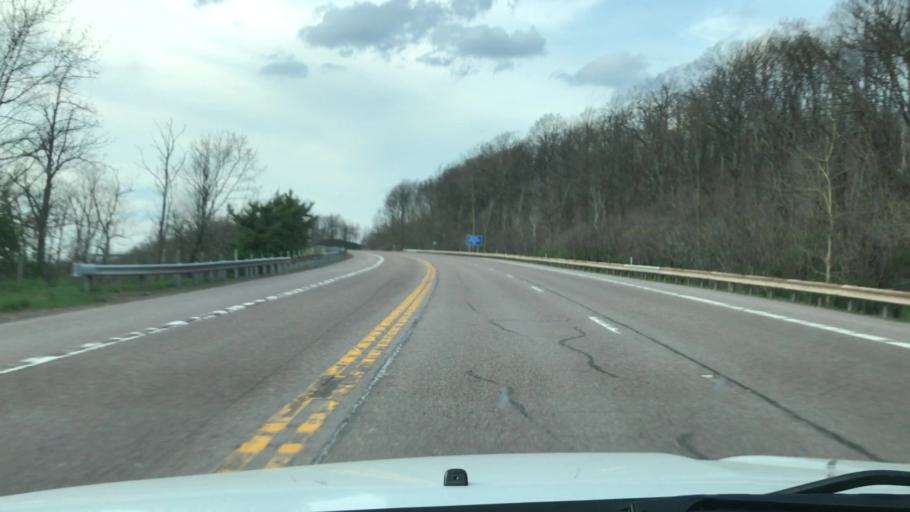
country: US
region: Maryland
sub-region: Garrett County
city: Mountain Lake Park
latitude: 39.6747
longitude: -79.2872
